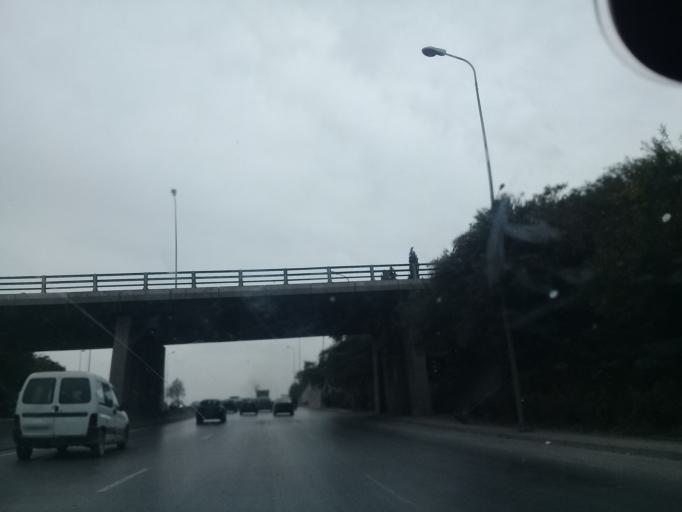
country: TN
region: Tunis
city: Tunis
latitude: 36.8334
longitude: 10.1559
